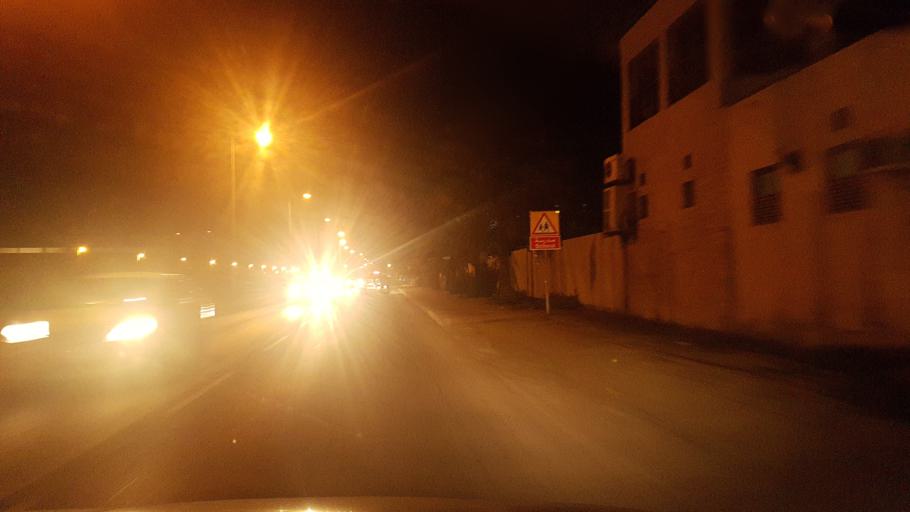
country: BH
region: Muharraq
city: Al Muharraq
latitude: 26.2794
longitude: 50.6309
